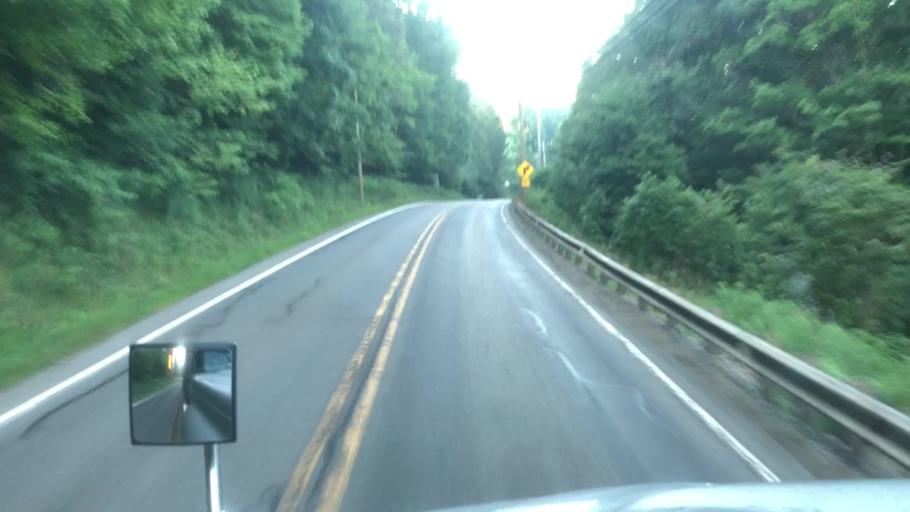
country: US
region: Pennsylvania
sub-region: Venango County
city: Hasson Heights
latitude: 41.4874
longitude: -79.6508
